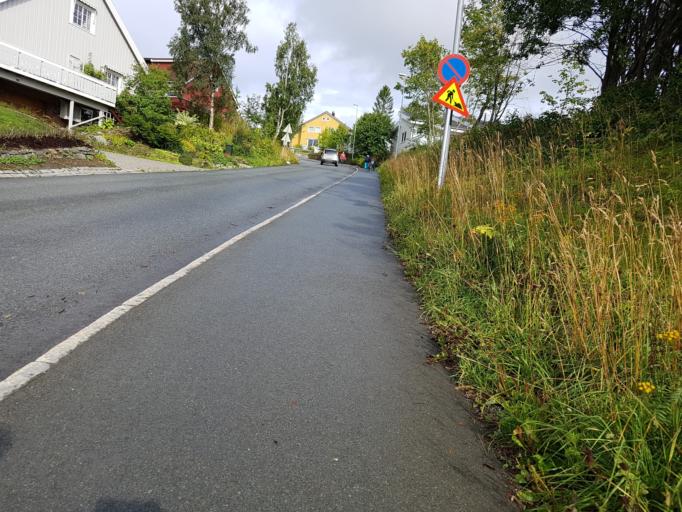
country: NO
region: Sor-Trondelag
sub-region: Trondheim
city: Trondheim
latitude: 63.4105
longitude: 10.4234
